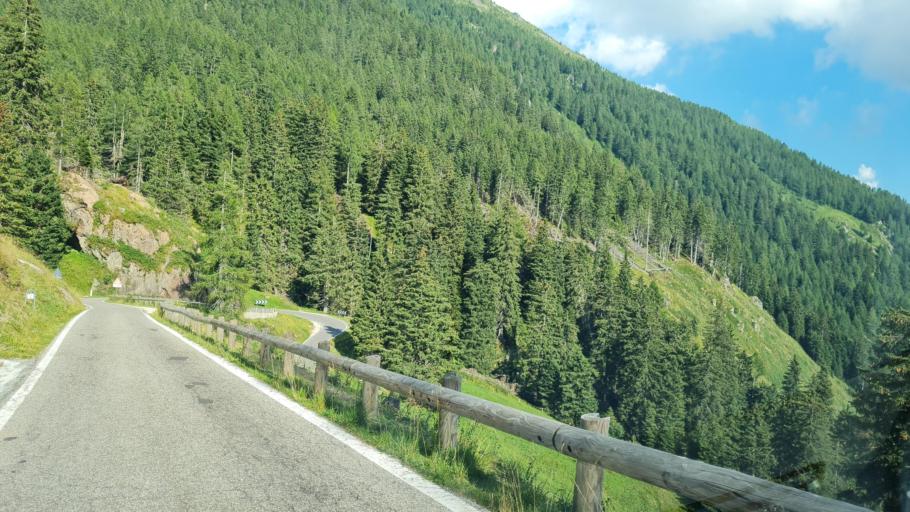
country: IT
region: Trentino-Alto Adige
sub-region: Provincia di Trento
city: Palu del Fersina
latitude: 46.1652
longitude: 11.4333
